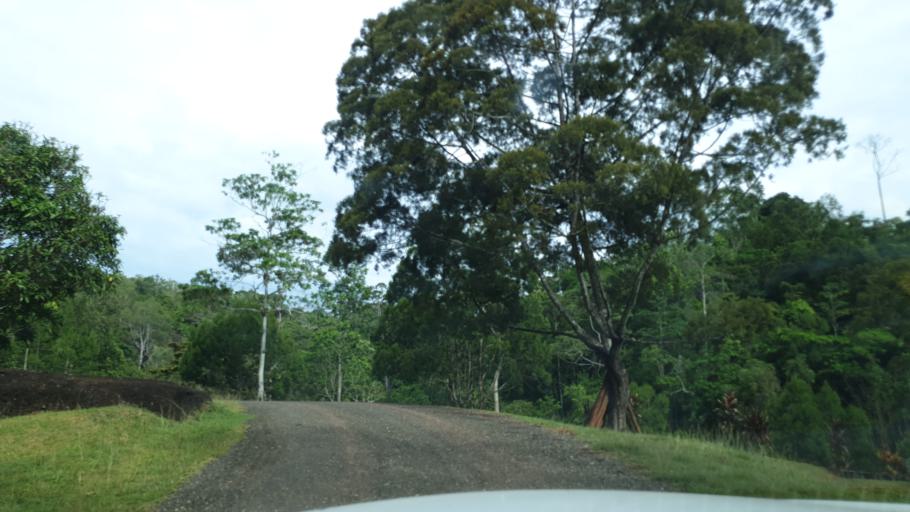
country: PG
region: National Capital
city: Port Moresby
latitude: -9.4360
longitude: 147.3938
